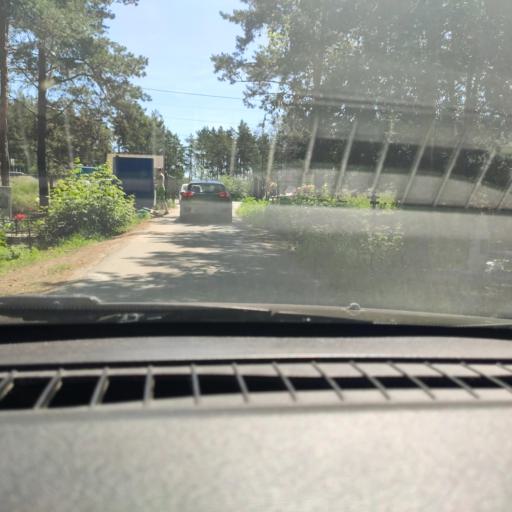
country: RU
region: Samara
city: Zhigulevsk
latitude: 53.5219
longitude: 49.5400
